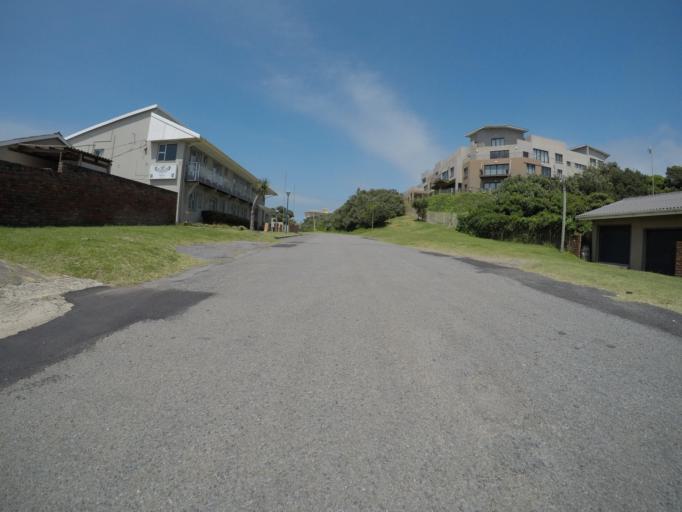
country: ZA
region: Eastern Cape
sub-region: Buffalo City Metropolitan Municipality
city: East London
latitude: -32.9401
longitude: 28.0331
